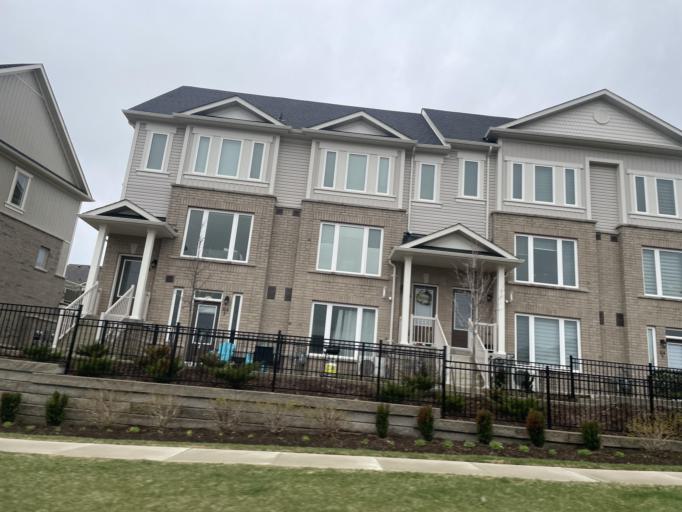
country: CA
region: Ontario
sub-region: Wellington County
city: Guelph
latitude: 43.5684
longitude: -80.2115
